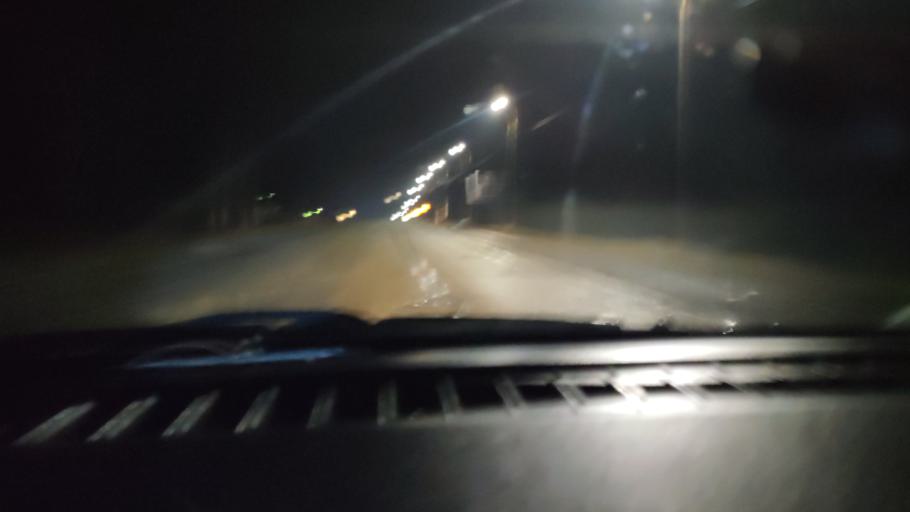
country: RU
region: Udmurtiya
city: Votkinsk
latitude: 57.0320
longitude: 53.9288
